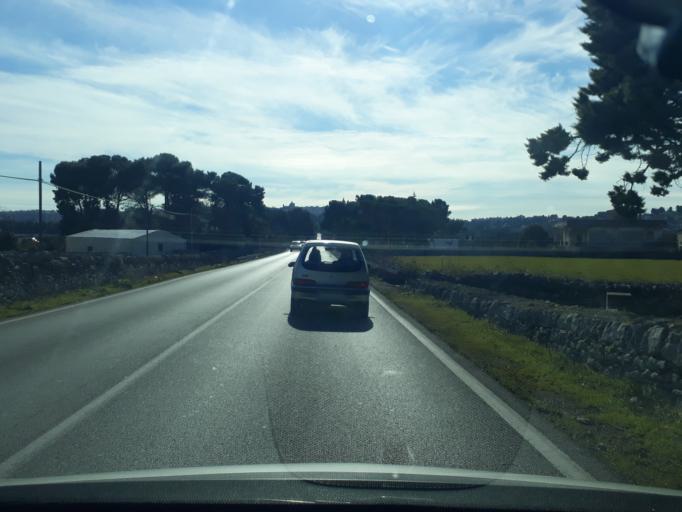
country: IT
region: Apulia
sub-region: Provincia di Taranto
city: Martina Franca
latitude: 40.7253
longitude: 17.3326
